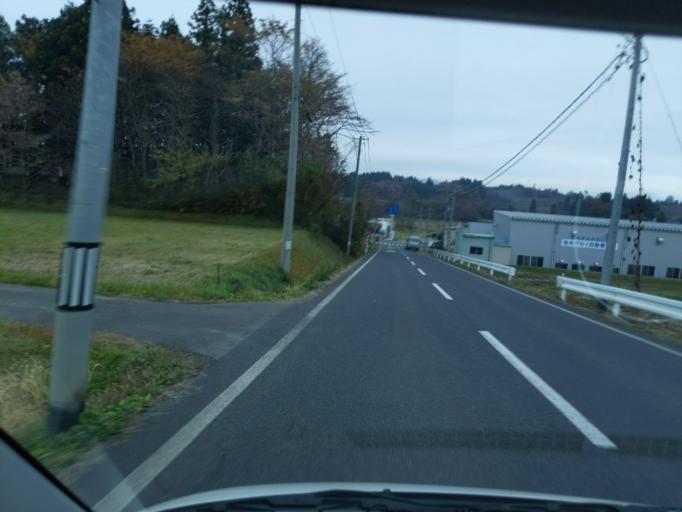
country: JP
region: Iwate
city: Kitakami
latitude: 39.2268
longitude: 141.2361
